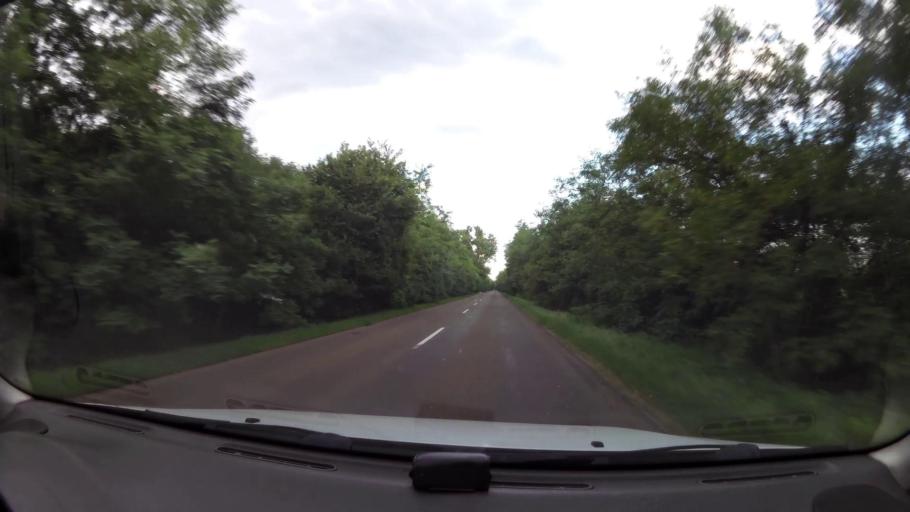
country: HU
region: Pest
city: Tapiosag
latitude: 47.3885
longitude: 19.6481
